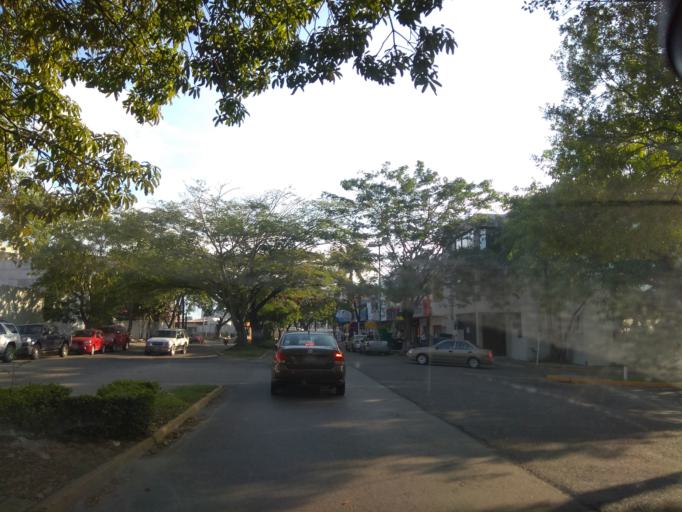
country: MX
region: Tabasco
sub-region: Nacajuca
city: Bosque de Saloya
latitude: 17.9995
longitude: -92.9494
